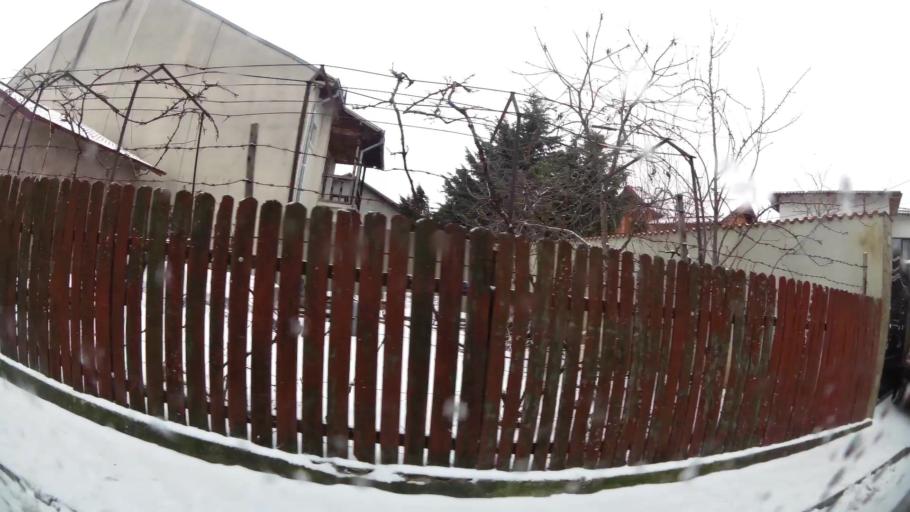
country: RO
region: Dambovita
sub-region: Municipiul Targoviste
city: Targoviste
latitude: 44.9247
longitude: 25.4755
